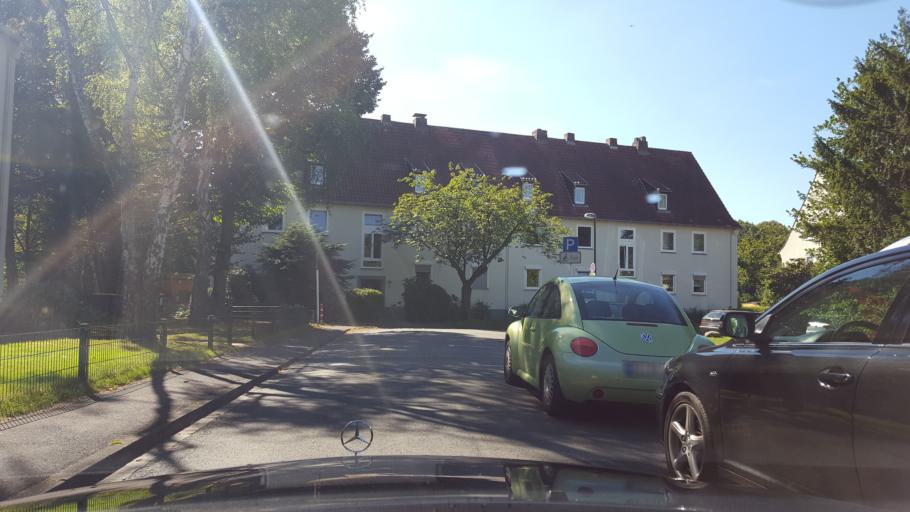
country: DE
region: North Rhine-Westphalia
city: Marl
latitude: 51.6741
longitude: 7.1118
